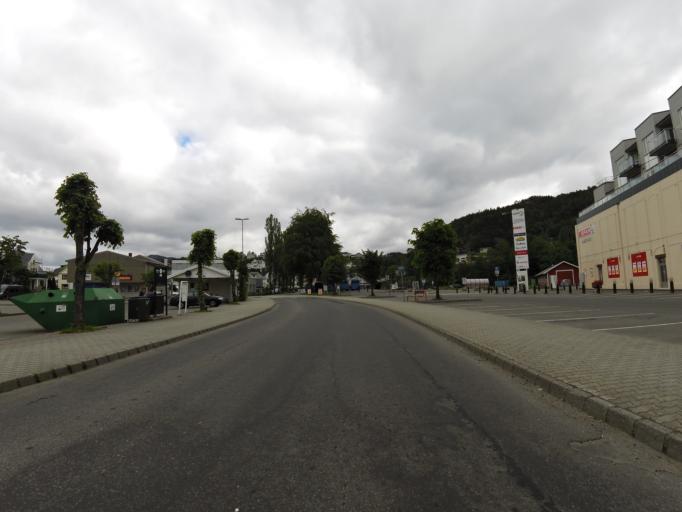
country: NO
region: Vest-Agder
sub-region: Flekkefjord
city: Flekkefjord
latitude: 58.2939
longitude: 6.6652
